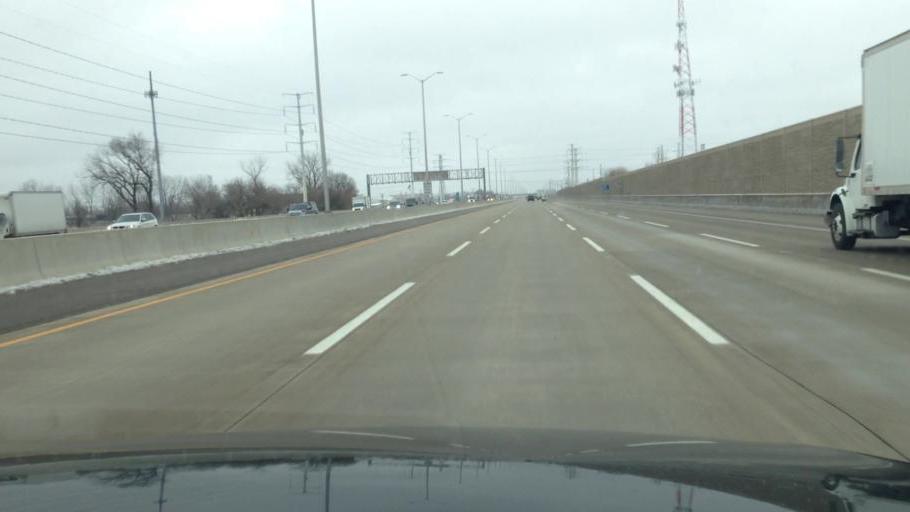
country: US
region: Illinois
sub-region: Kane County
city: East Dundee
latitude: 42.0680
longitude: -88.2470
